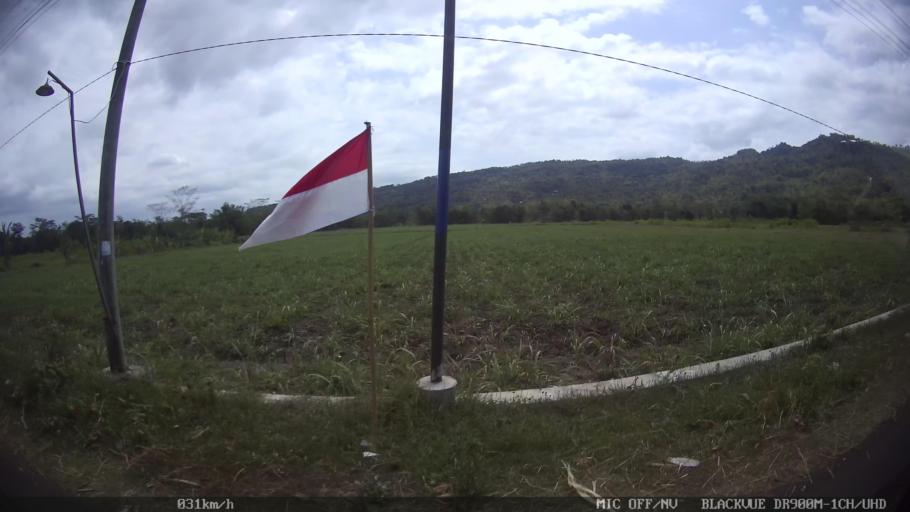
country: ID
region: Central Java
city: Candi Prambanan
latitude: -7.8113
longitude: 110.5073
